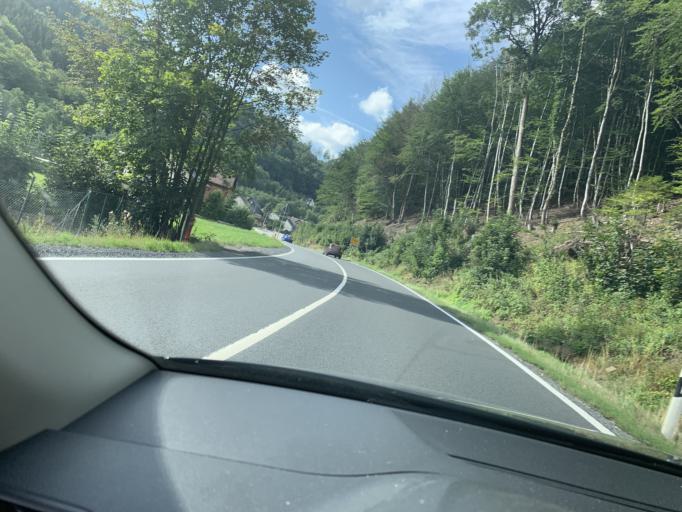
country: DE
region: Thuringia
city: Judenbach
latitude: 50.3790
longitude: 11.2010
